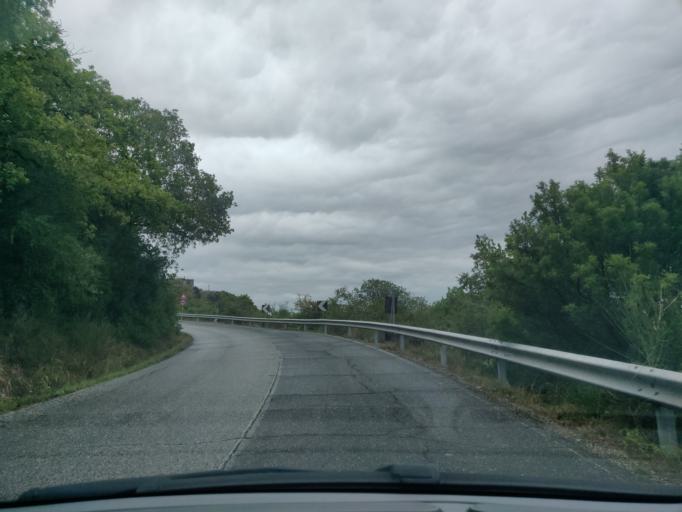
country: IT
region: Latium
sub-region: Citta metropolitana di Roma Capitale
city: Allumiere
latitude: 42.1293
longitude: 11.8519
